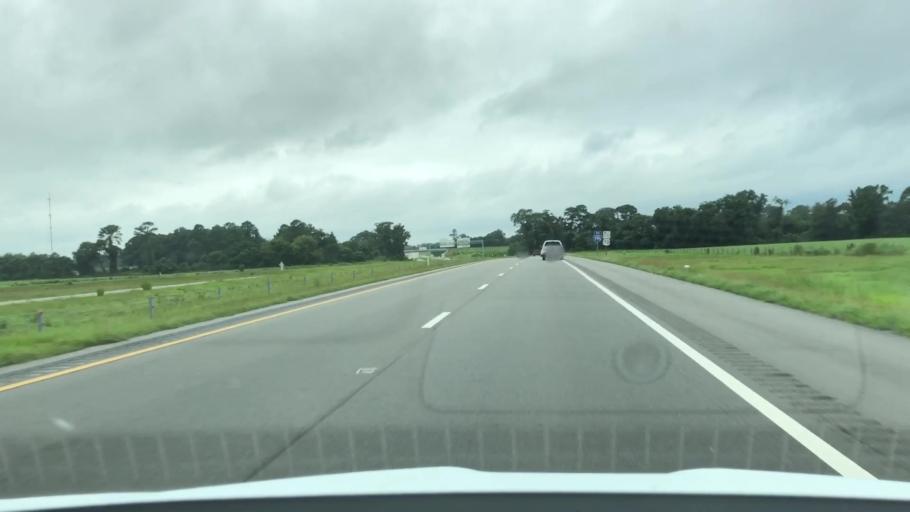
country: US
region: North Carolina
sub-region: Lenoir County
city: La Grange
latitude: 35.3058
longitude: -77.8200
